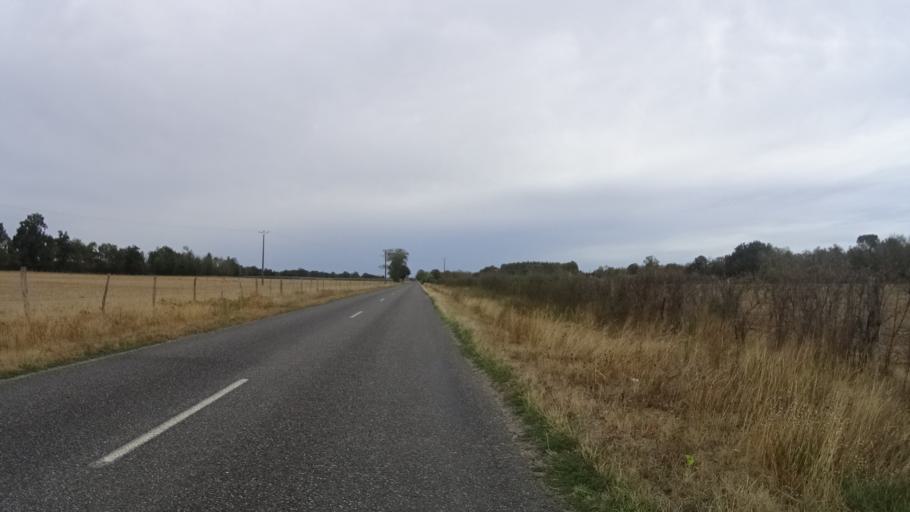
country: FR
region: Bourgogne
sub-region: Departement de la Nievre
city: Lucenay-les-Aix
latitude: 46.7639
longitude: 3.5604
